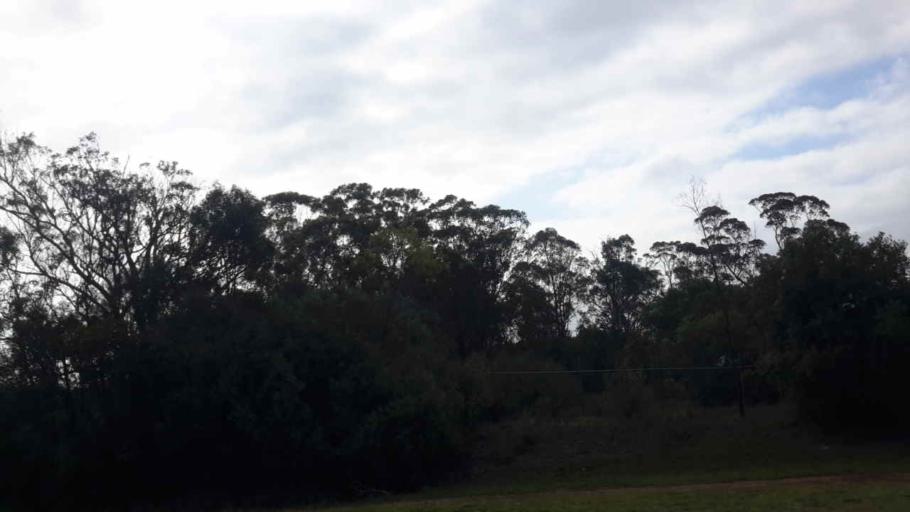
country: AU
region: New South Wales
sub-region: Campbelltown Municipality
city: Glen Alpine
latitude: -34.0896
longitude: 150.7733
